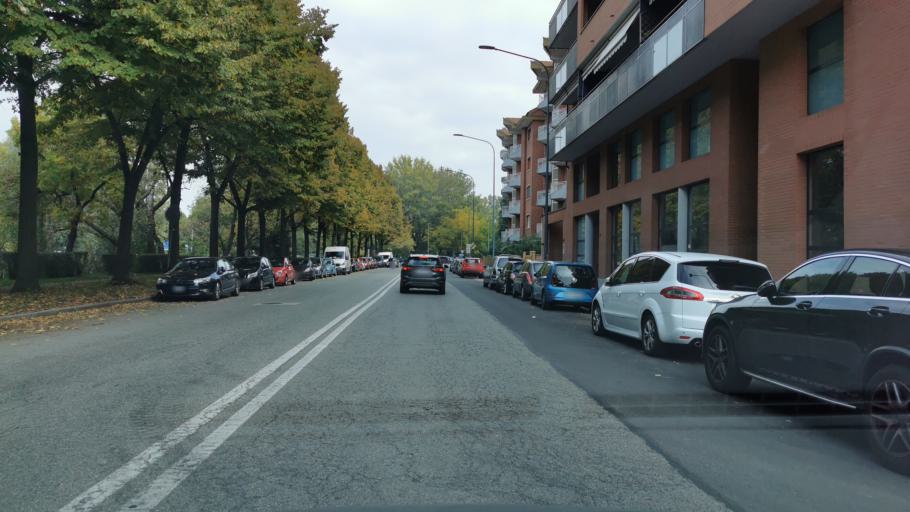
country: IT
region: Piedmont
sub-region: Provincia di Torino
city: Turin
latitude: 45.0744
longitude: 7.7166
